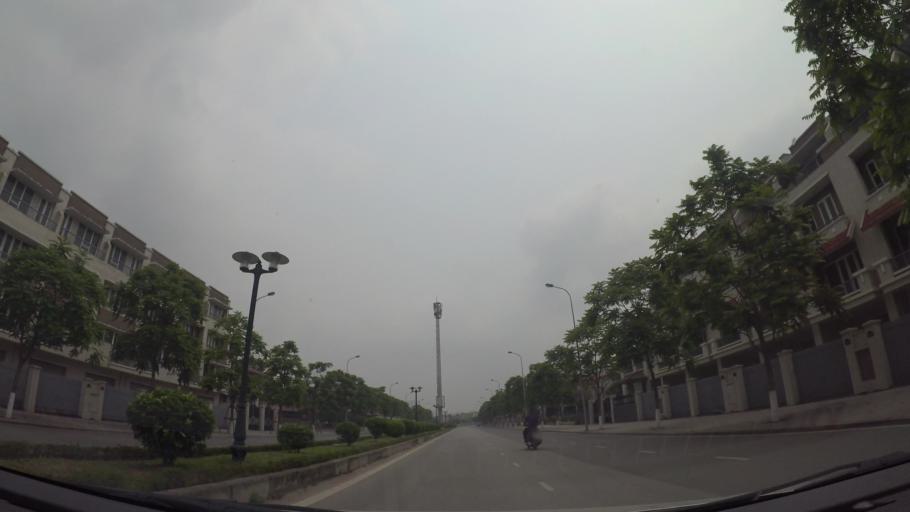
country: VN
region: Ha Noi
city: Ha Dong
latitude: 20.9747
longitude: 105.7548
